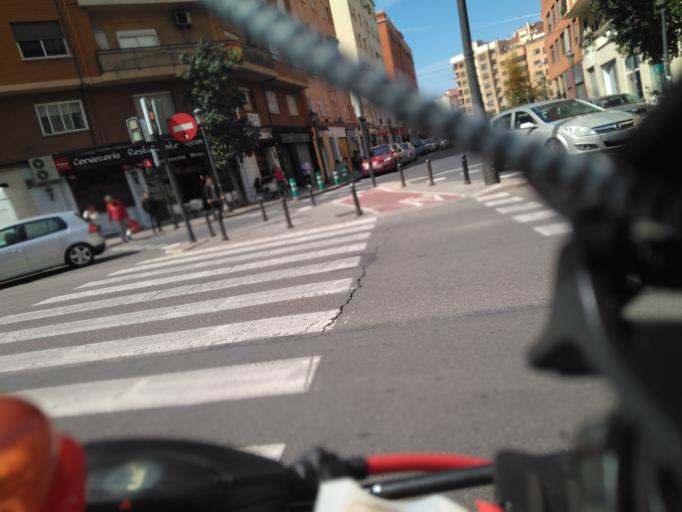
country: ES
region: Valencia
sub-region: Provincia de Valencia
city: Valencia
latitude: 39.4711
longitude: -0.3930
